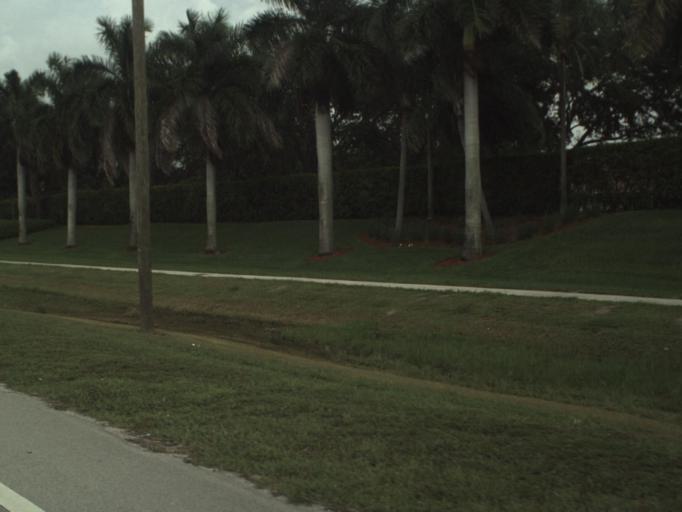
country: US
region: Florida
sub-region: Palm Beach County
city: Royal Palm Beach
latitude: 26.7091
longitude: -80.1876
